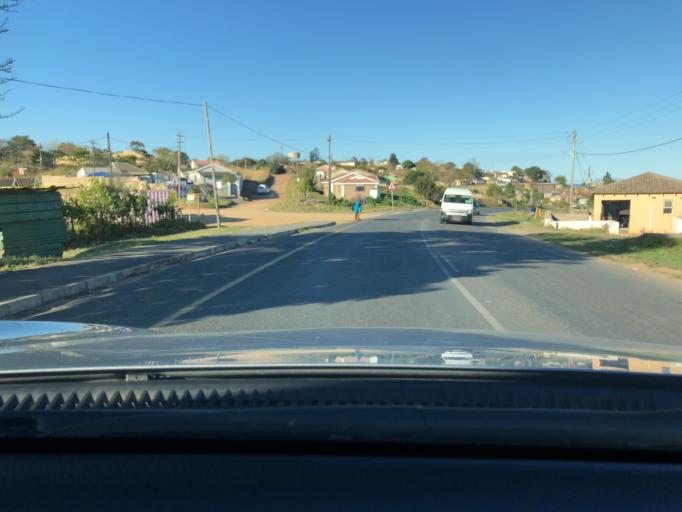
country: ZA
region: KwaZulu-Natal
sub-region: eThekwini Metropolitan Municipality
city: Umkomaas
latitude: -30.0345
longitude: 30.8423
